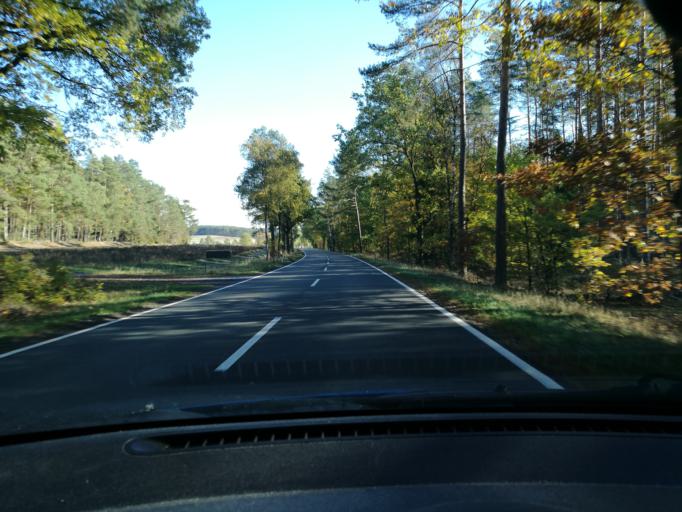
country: DE
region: Lower Saxony
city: Nahrendorf
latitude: 53.1510
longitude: 10.8378
